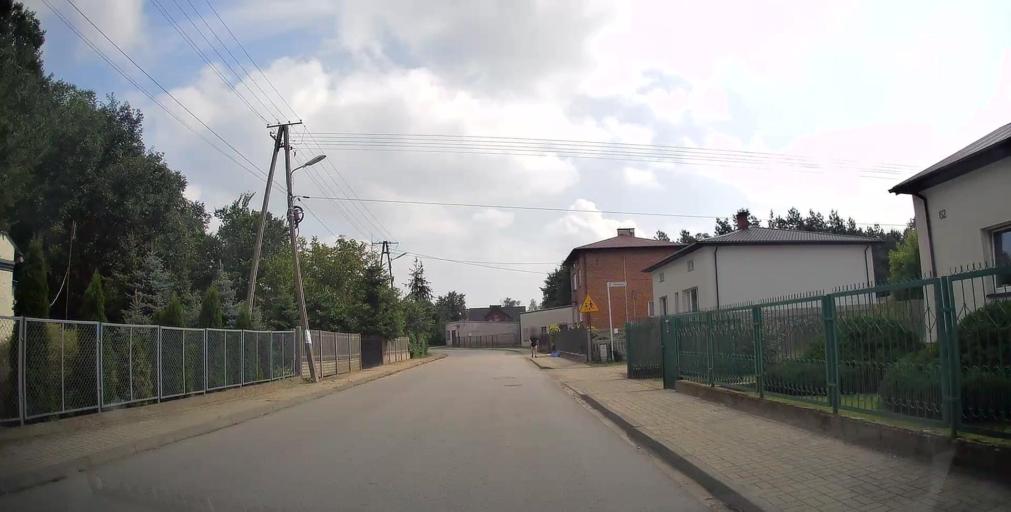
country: PL
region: Masovian Voivodeship
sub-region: Powiat bialobrzeski
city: Sucha
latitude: 51.6188
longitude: 20.9524
